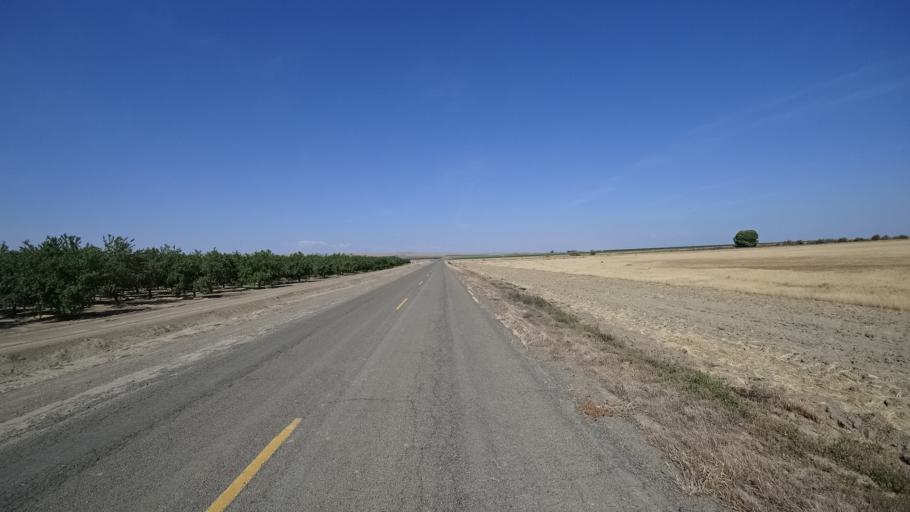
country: US
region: California
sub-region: Kings County
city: Kettleman City
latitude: 36.0364
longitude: -119.9643
